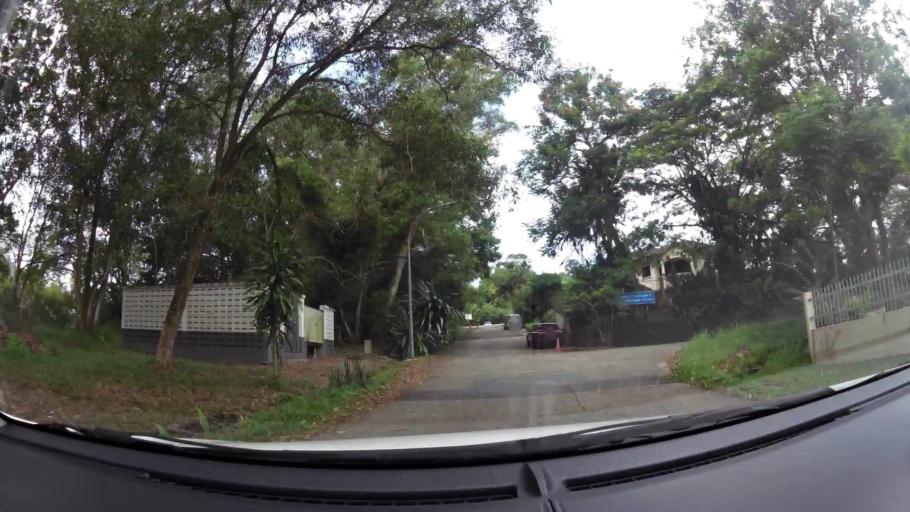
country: BN
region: Brunei and Muara
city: Bandar Seri Begawan
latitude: 4.8718
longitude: 114.8999
